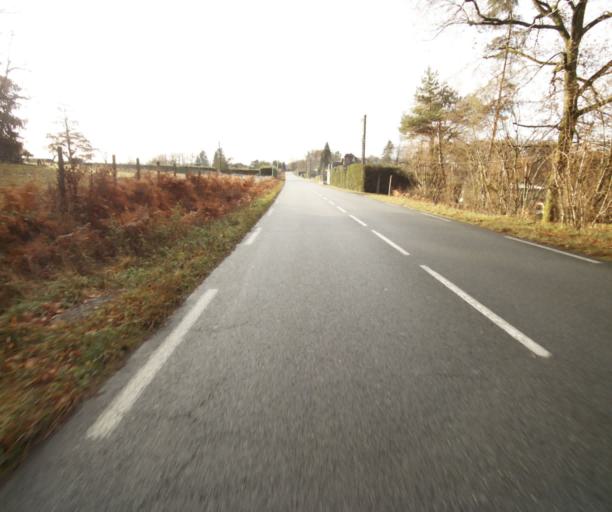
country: FR
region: Limousin
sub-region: Departement de la Correze
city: Saint-Mexant
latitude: 45.2606
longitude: 1.6356
